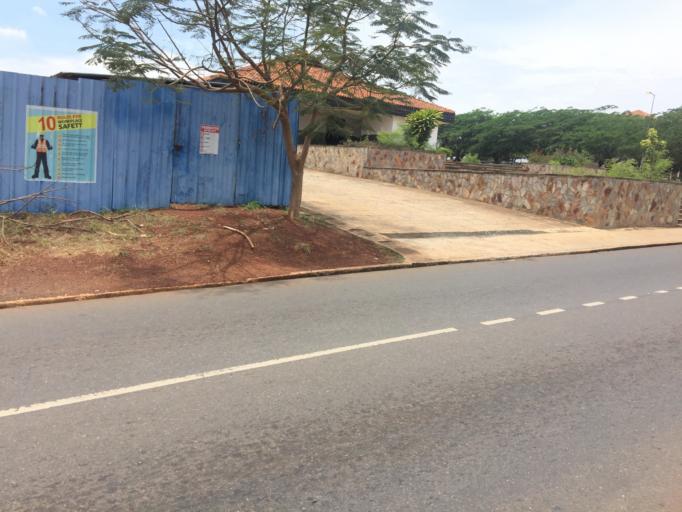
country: GH
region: Greater Accra
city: Medina Estates
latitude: 5.6527
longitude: -0.1825
